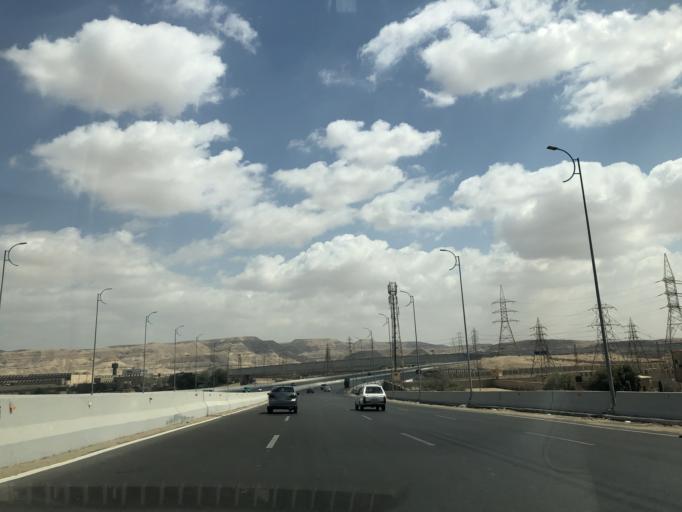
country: EG
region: Muhafazat al Qahirah
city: Halwan
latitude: 29.8765
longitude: 31.3192
